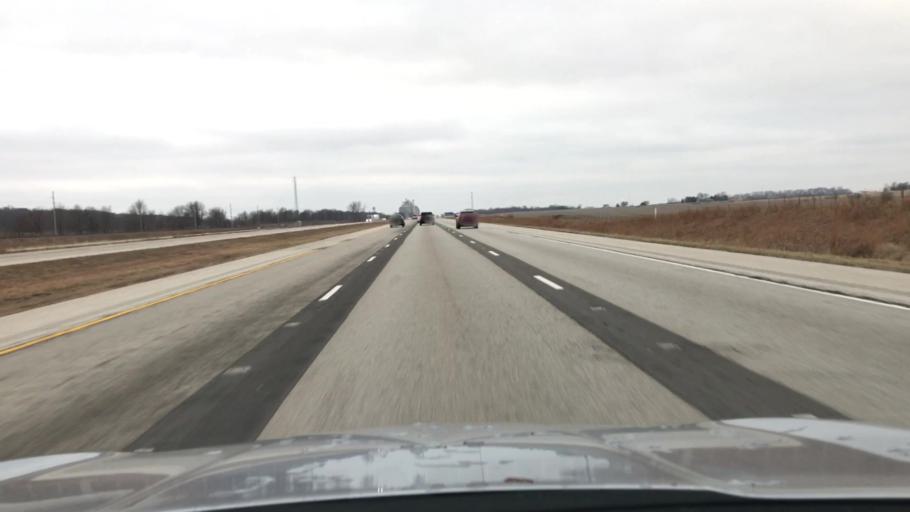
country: US
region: Illinois
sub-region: Sangamon County
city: Williamsville
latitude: 40.0390
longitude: -89.4687
